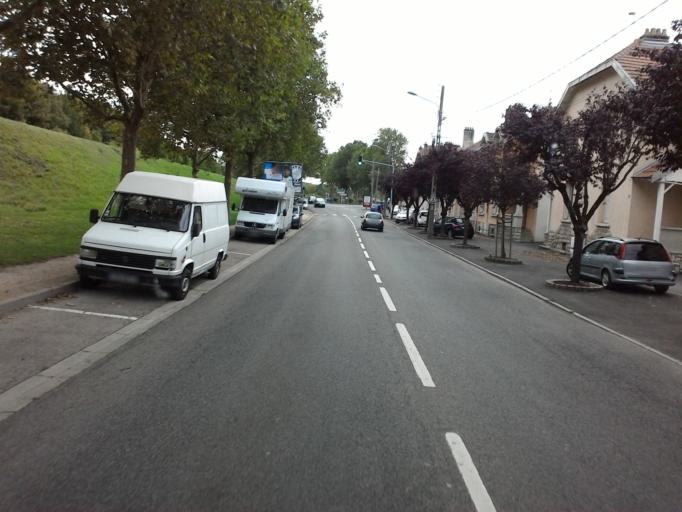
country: FR
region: Lorraine
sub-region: Departement de Meurthe-et-Moselle
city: Toul
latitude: 48.6777
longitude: 5.8970
